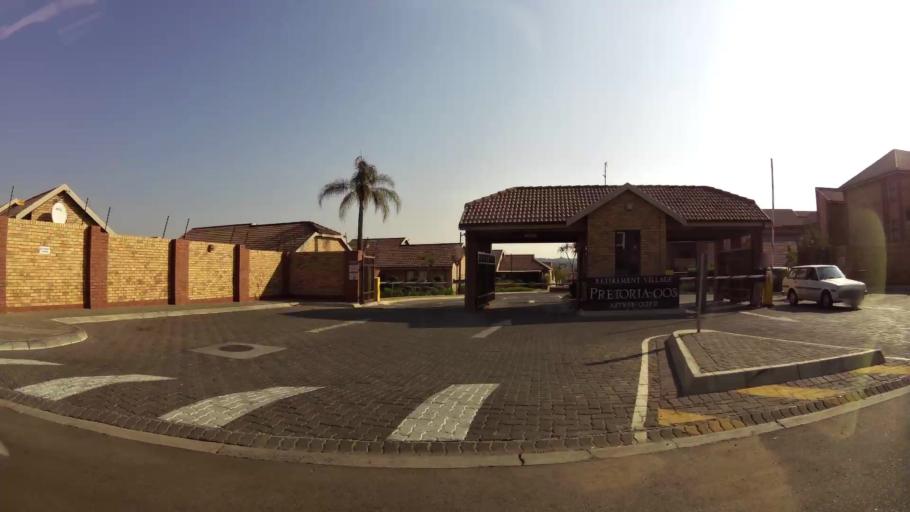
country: ZA
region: Gauteng
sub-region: City of Tshwane Metropolitan Municipality
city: Pretoria
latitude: -25.7637
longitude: 28.3271
